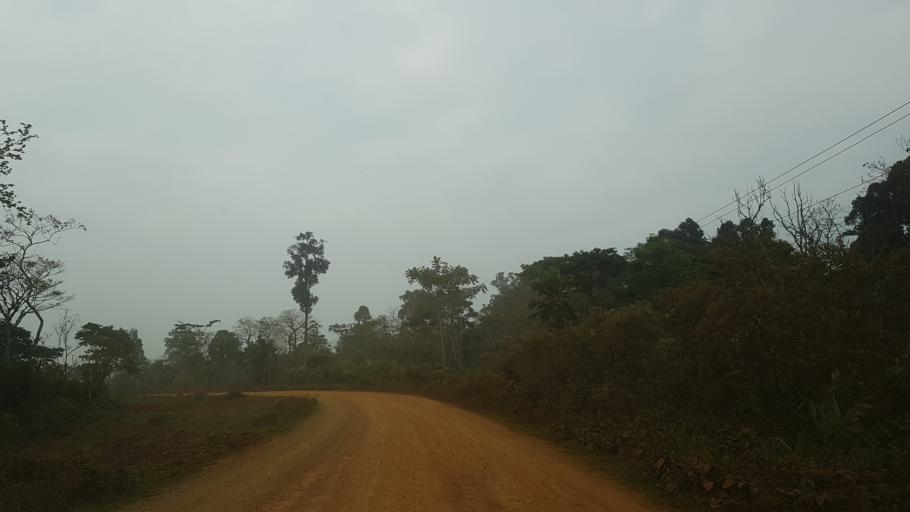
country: ET
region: Oromiya
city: Gore
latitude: 7.8896
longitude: 35.4859
